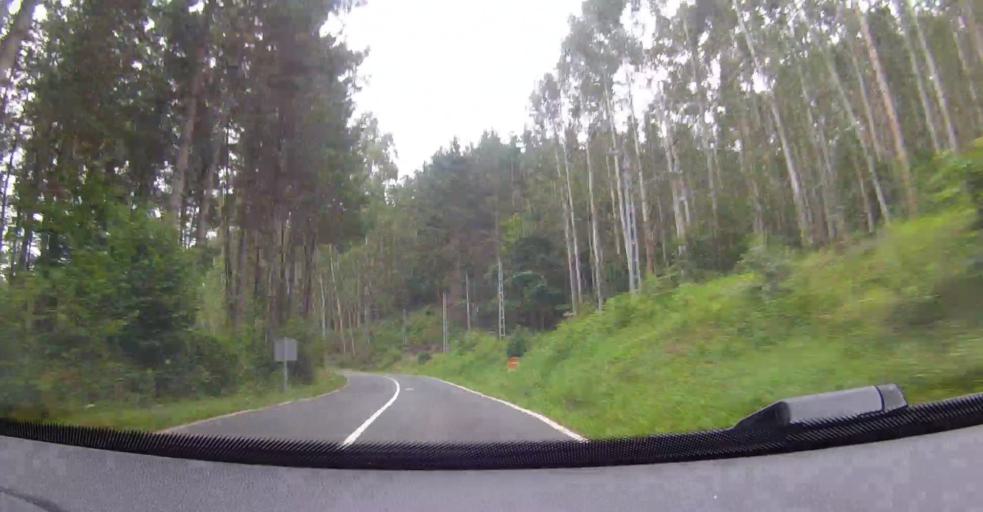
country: ES
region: Basque Country
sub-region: Bizkaia
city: Balmaseda
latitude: 43.2399
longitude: -3.2414
